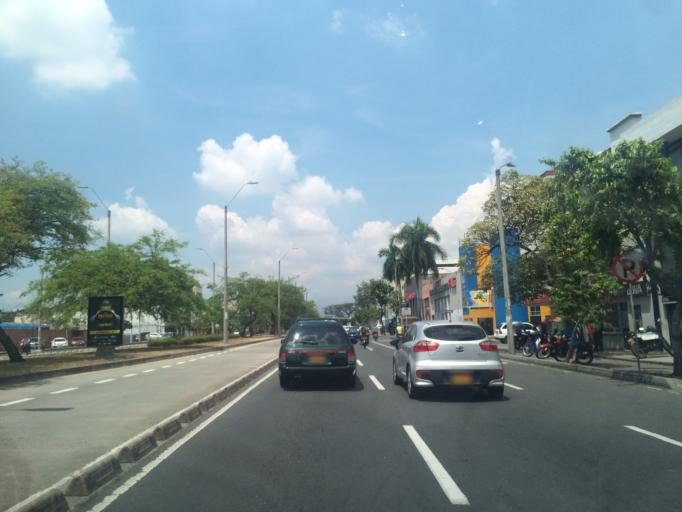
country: CO
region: Valle del Cauca
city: Cali
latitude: 3.4689
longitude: -76.5114
